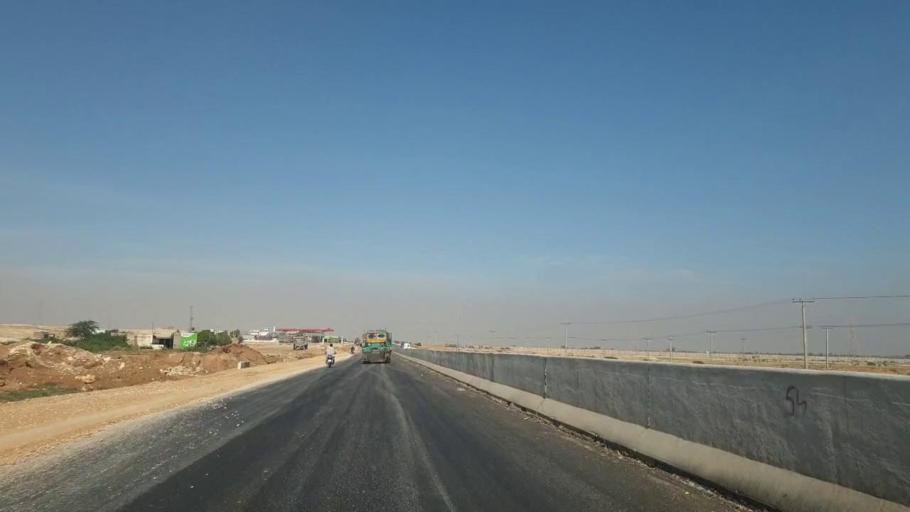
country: PK
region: Sindh
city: Jamshoro
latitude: 25.4967
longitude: 68.2724
